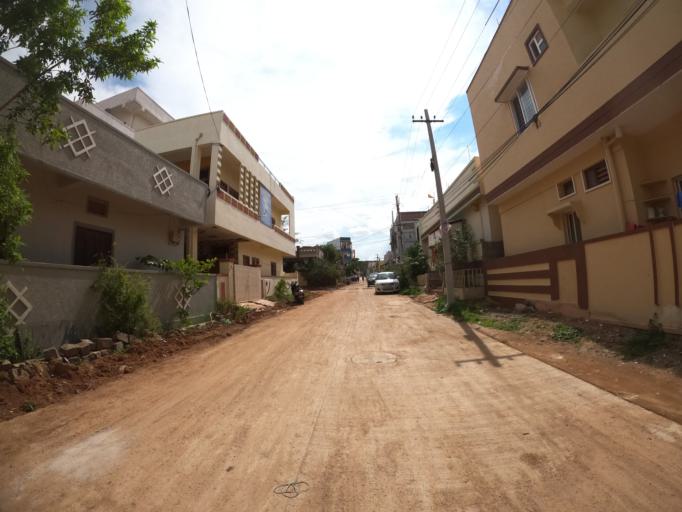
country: IN
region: Telangana
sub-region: Hyderabad
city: Hyderabad
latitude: 17.3629
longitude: 78.3830
